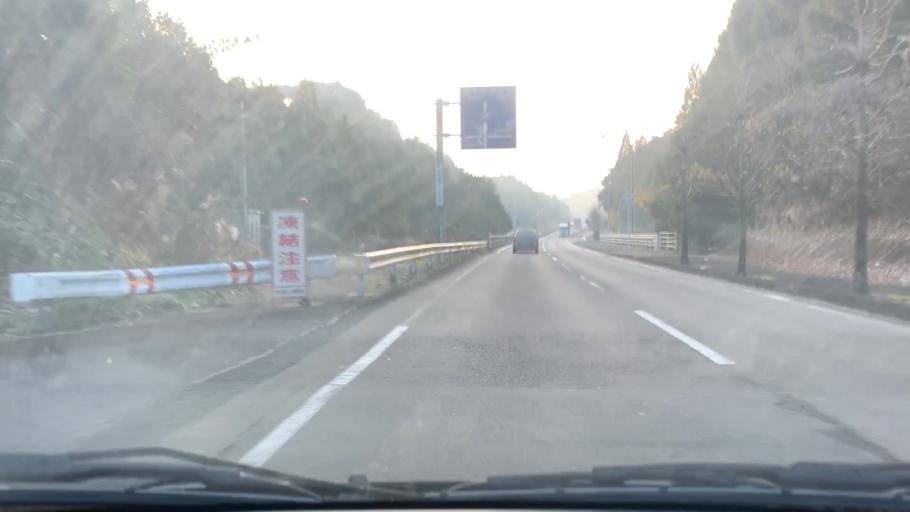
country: JP
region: Saga Prefecture
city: Imaricho-ko
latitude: 33.2642
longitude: 129.9473
